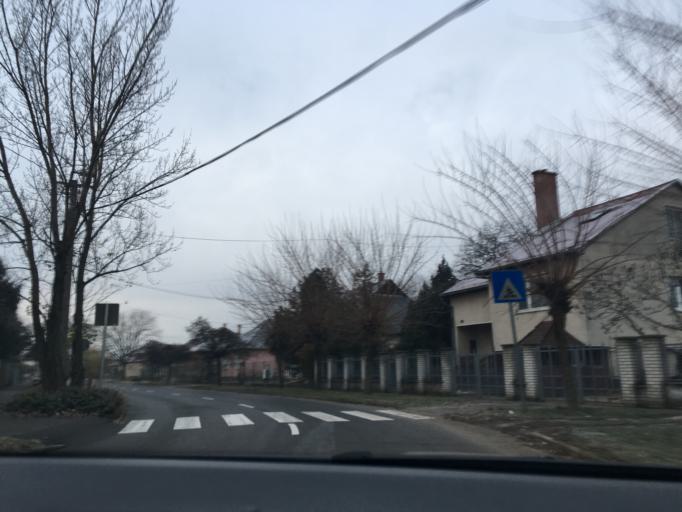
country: HU
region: Hajdu-Bihar
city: Debrecen
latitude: 47.5387
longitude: 21.6541
